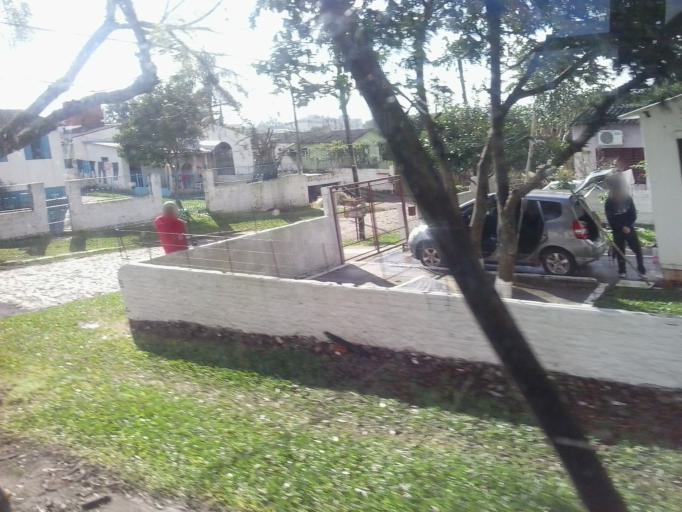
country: BR
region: Rio Grande do Sul
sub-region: Santa Maria
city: Santa Maria
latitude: -29.7110
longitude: -53.7270
